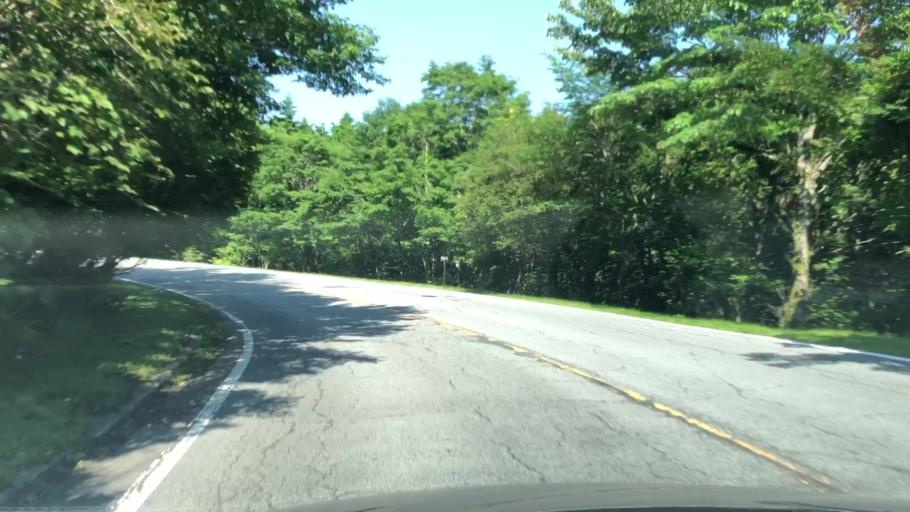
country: JP
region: Shizuoka
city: Gotemba
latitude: 35.3215
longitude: 138.7956
